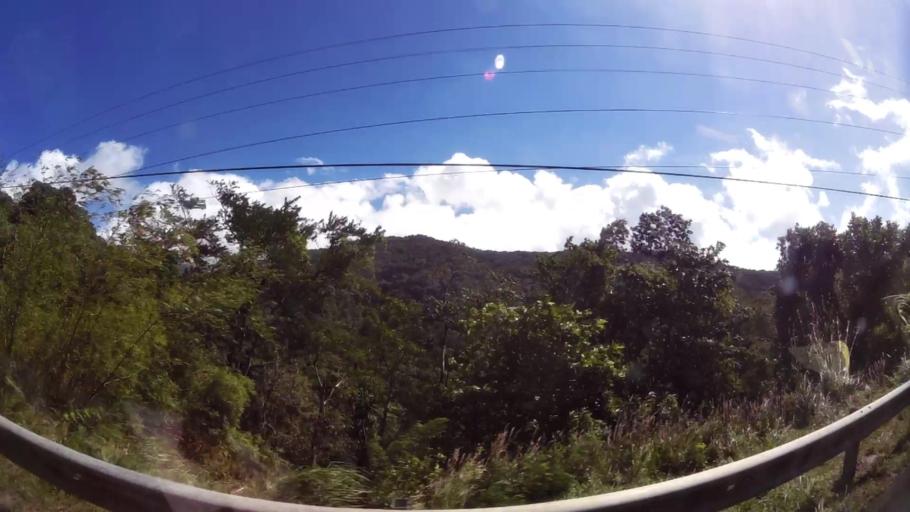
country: DM
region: Saint Paul
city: Pont Casse
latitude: 15.3493
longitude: -61.3618
